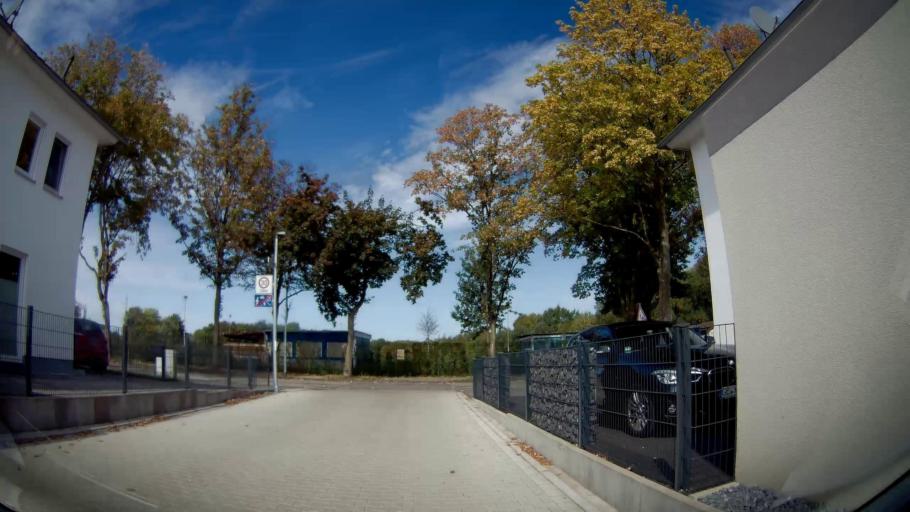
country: DE
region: North Rhine-Westphalia
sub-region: Regierungsbezirk Munster
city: Gladbeck
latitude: 51.5485
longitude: 7.0323
